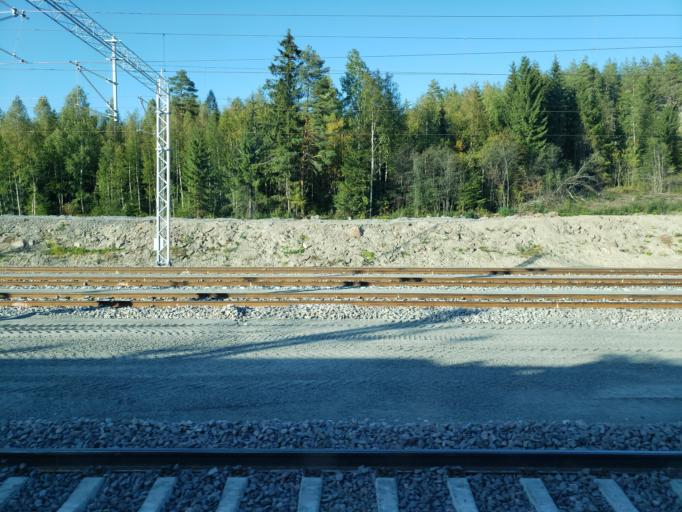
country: FI
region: South Karelia
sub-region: Lappeenranta
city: Lappeenranta
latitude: 60.8598
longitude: 28.3210
